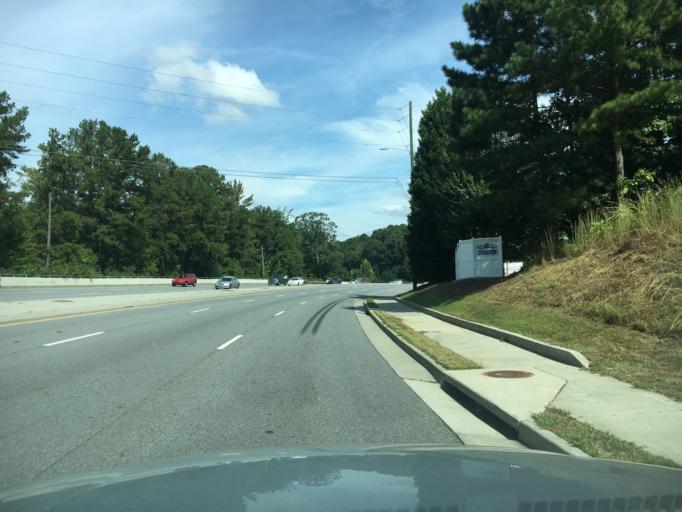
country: US
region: Georgia
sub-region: Gwinnett County
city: Duluth
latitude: 33.9886
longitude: -84.1611
